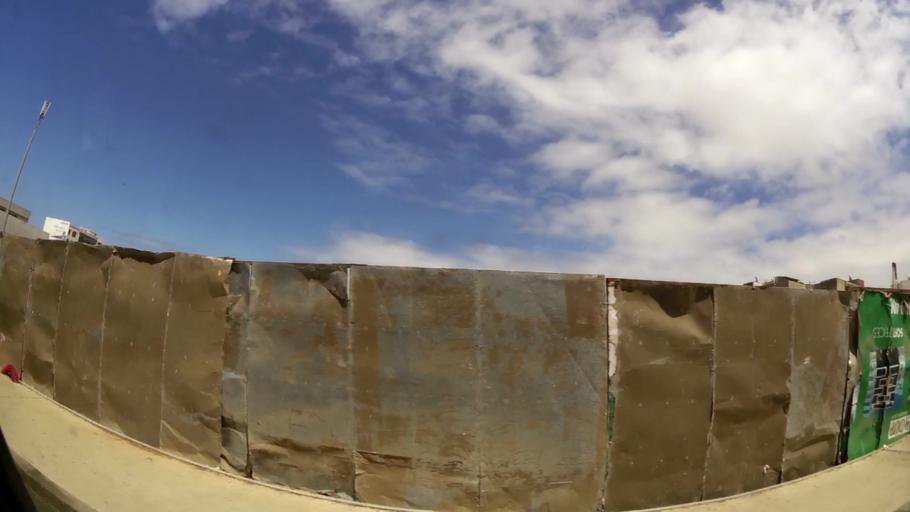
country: MA
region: Grand Casablanca
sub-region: Mediouna
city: Tit Mellil
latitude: 33.6049
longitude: -7.5271
